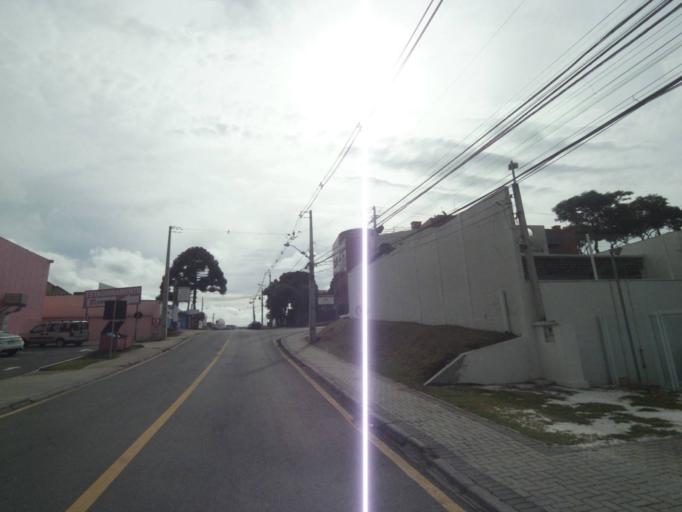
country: BR
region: Parana
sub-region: Curitiba
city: Curitiba
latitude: -25.4400
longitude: -49.3071
